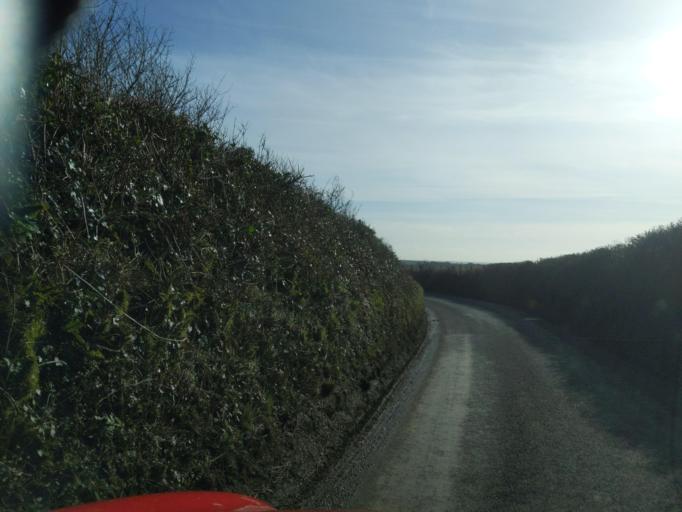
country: GB
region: England
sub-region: Devon
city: Kingsbridge
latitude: 50.3414
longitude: -3.7244
